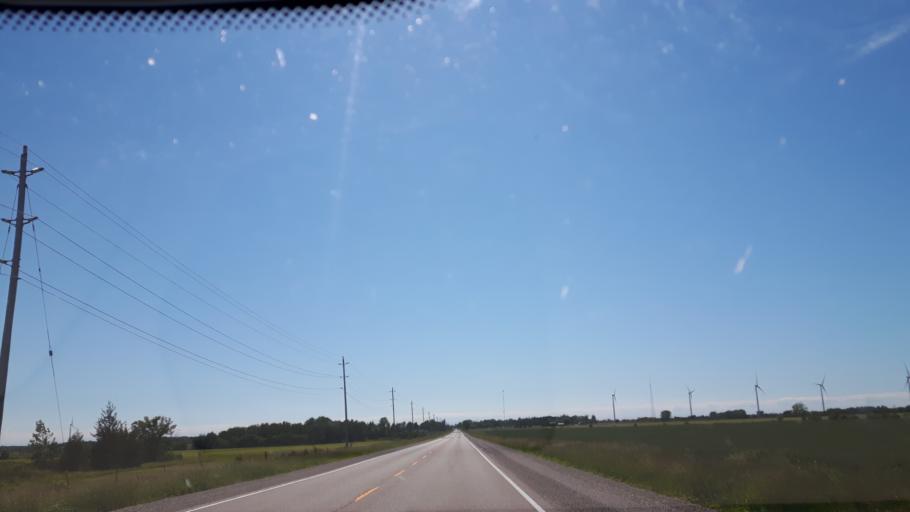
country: CA
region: Ontario
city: Bluewater
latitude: 43.4178
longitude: -81.6577
